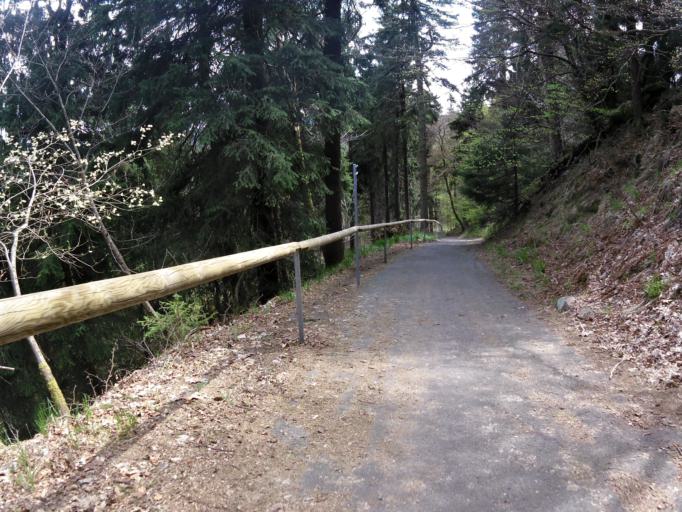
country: DE
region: Thuringia
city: Brotterode
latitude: 50.8488
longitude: 10.4728
